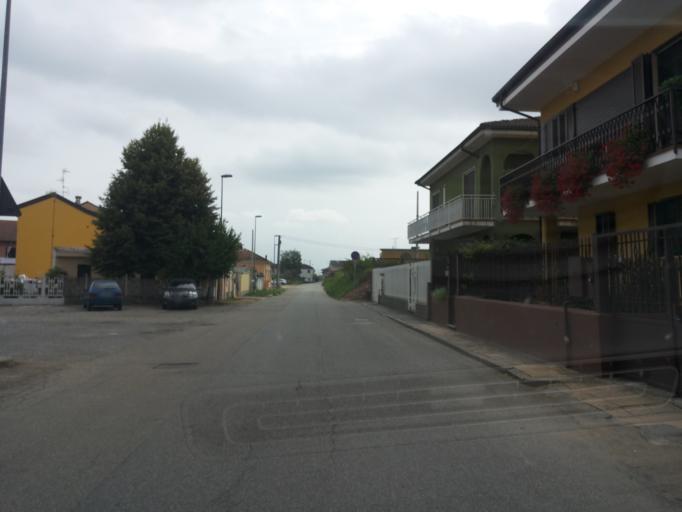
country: IT
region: Piedmont
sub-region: Provincia di Vercelli
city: Prarolo
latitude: 45.3046
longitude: 8.4517
